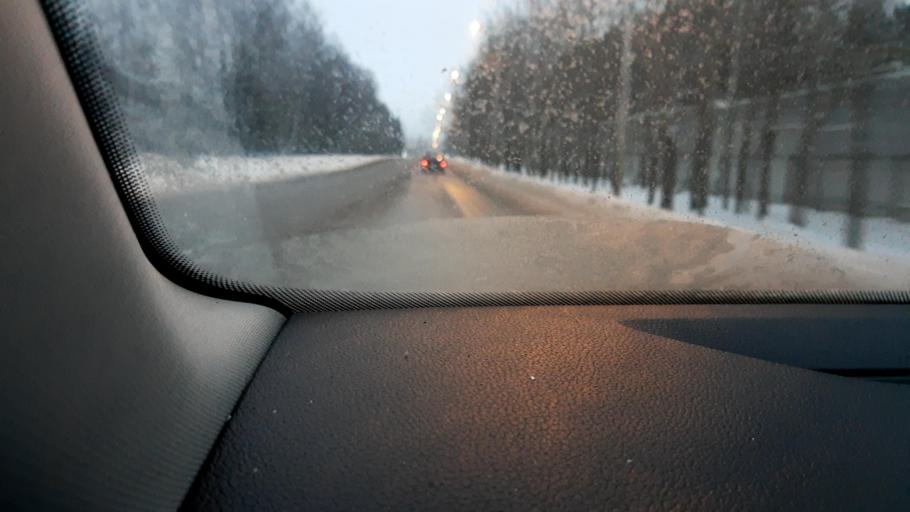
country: RU
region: Moskovskaya
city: Troitsk
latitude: 55.3036
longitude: 37.1967
